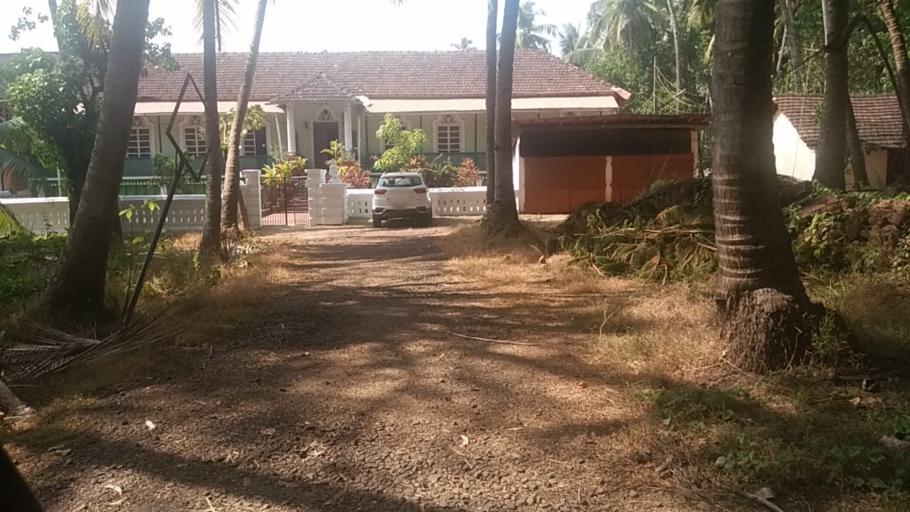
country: IN
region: Goa
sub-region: South Goa
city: Sancoale
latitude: 15.3384
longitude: 73.8980
